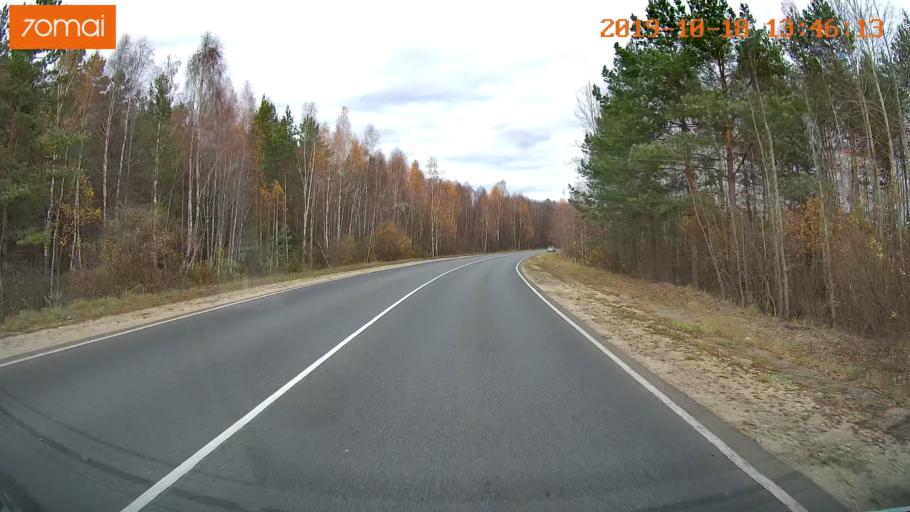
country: RU
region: Rjazan
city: Solotcha
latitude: 54.9578
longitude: 39.9389
